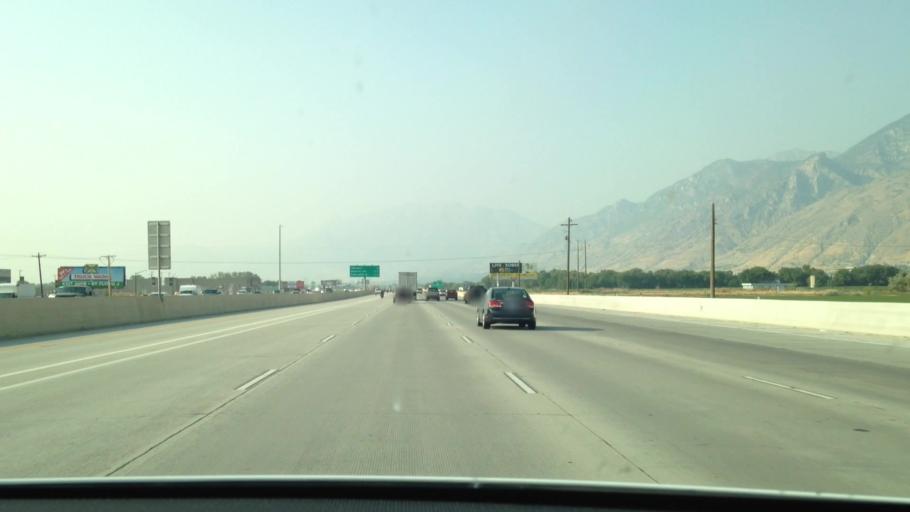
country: US
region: Utah
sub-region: Utah County
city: Springville
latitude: 40.1716
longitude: -111.6465
